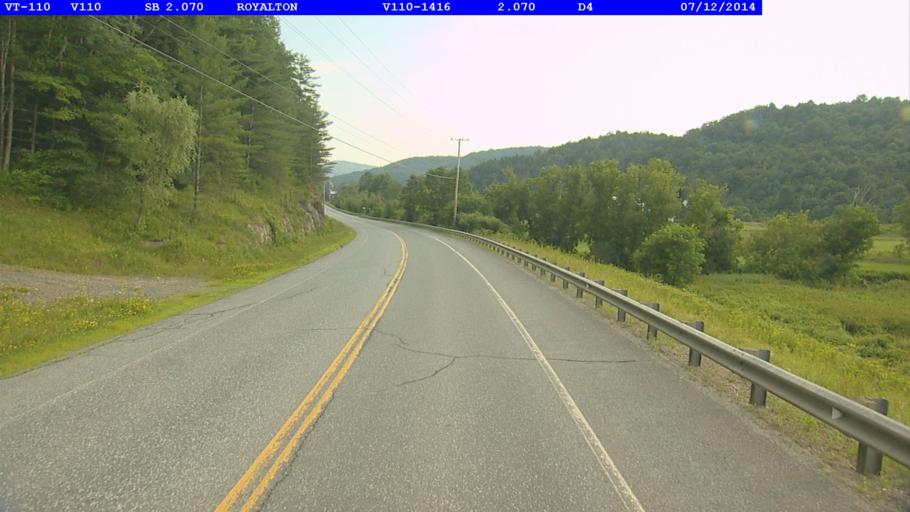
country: US
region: Vermont
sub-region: Orange County
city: Chelsea
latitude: 43.8500
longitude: -72.5101
